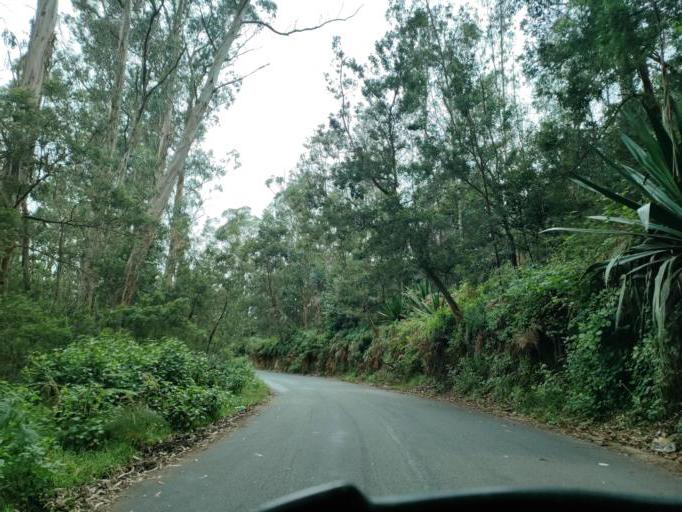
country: IN
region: Tamil Nadu
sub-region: Dindigul
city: Kodaikanal
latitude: 10.2408
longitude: 77.3681
